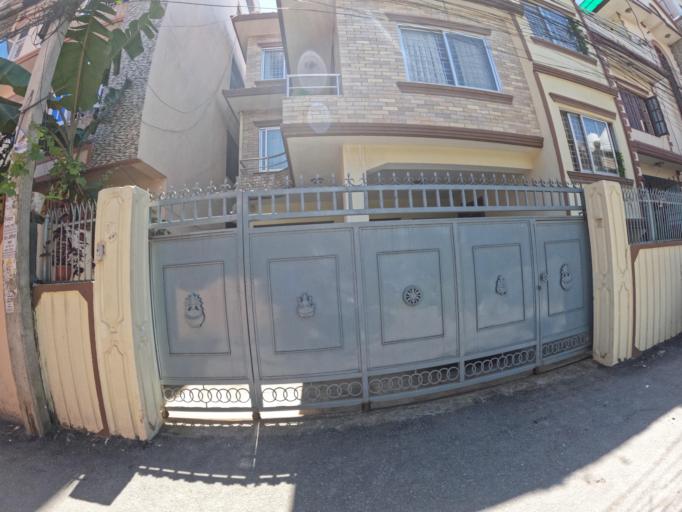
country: NP
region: Central Region
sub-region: Bagmati Zone
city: Kathmandu
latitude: 27.7372
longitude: 85.3216
